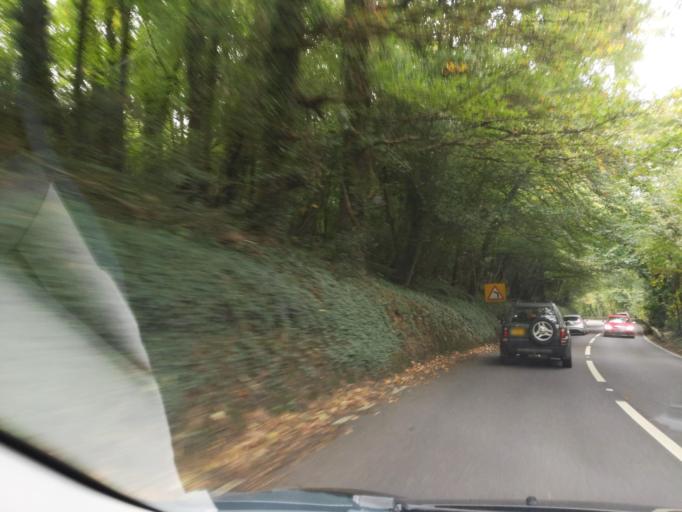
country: GB
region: England
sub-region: Cornwall
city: Wadebridge
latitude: 50.5058
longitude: -4.7811
